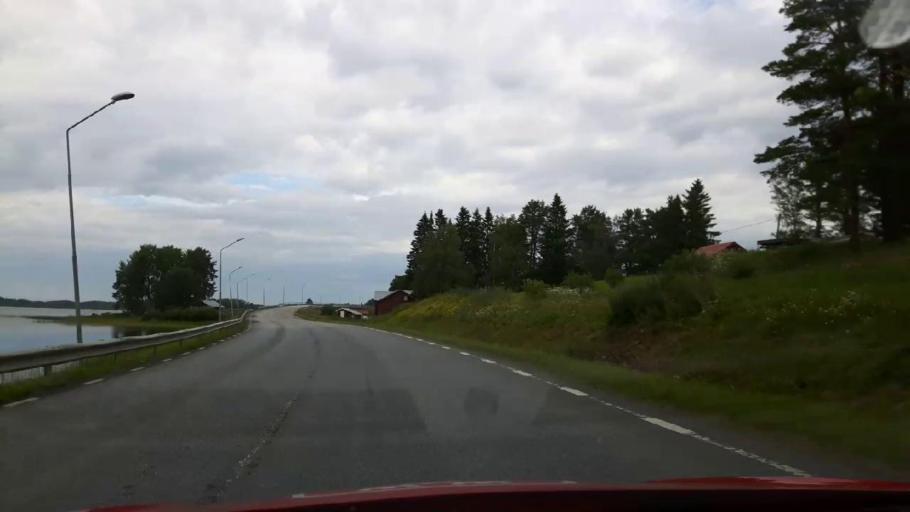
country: SE
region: Jaemtland
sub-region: Stroemsunds Kommun
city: Stroemsund
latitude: 63.5978
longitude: 15.3561
